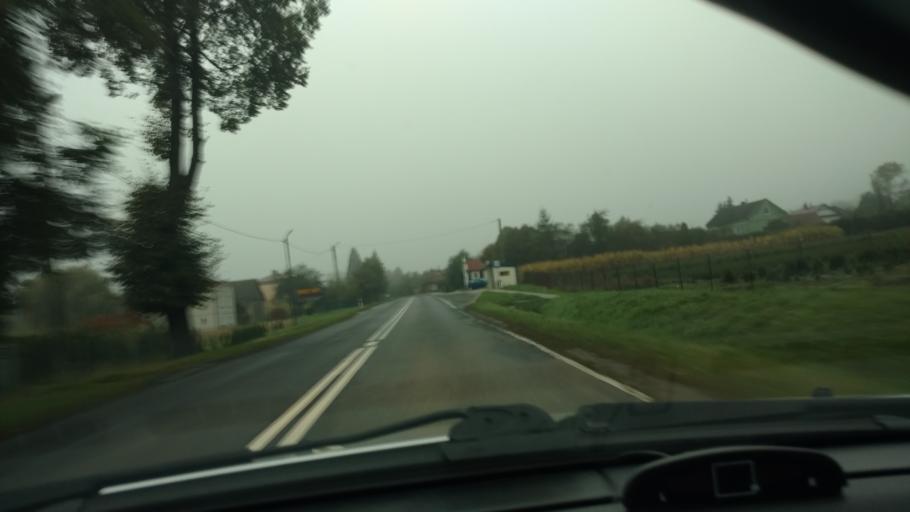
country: PL
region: Subcarpathian Voivodeship
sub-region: Powiat strzyzowski
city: Wisniowa
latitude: 49.8753
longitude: 21.6991
